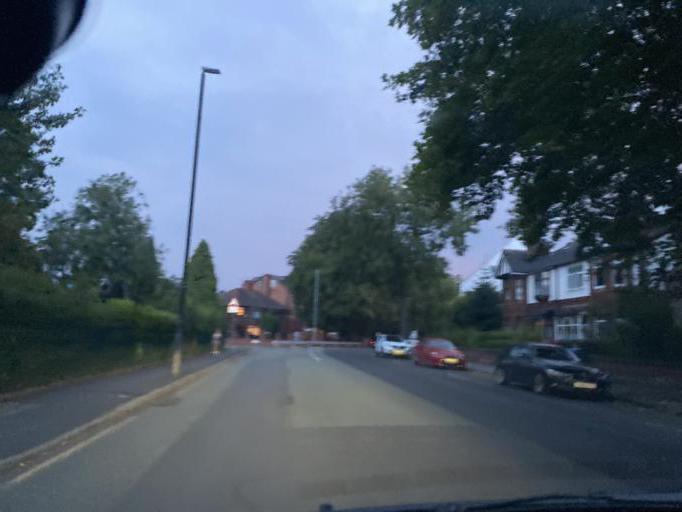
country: GB
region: England
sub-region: Manchester
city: Chorlton cum Hardy
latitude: 53.4511
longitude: -2.2709
